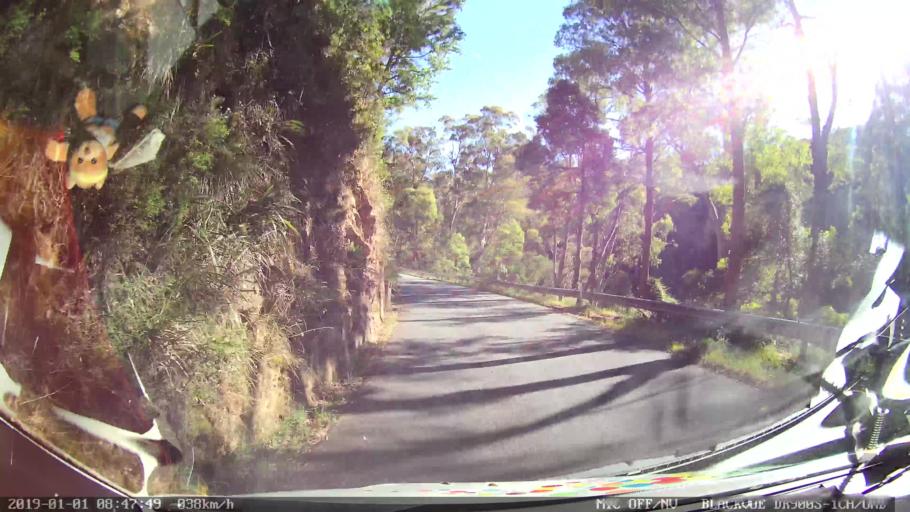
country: AU
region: New South Wales
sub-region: Snowy River
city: Jindabyne
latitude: -36.2924
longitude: 148.1987
